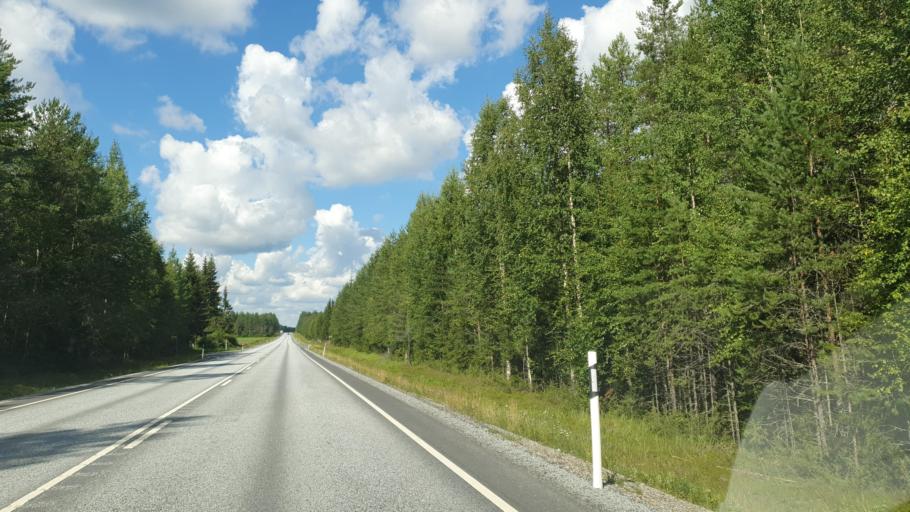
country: FI
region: Northern Savo
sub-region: Ylae-Savo
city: Sonkajaervi
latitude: 63.8897
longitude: 27.4271
